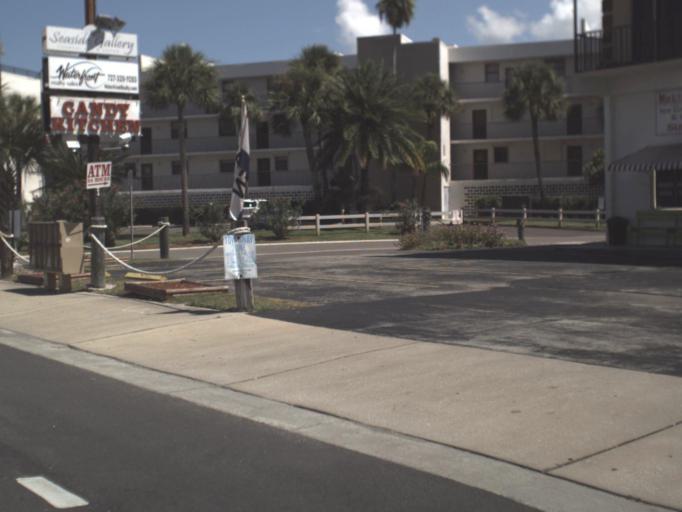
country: US
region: Florida
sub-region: Pinellas County
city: Redington Shores
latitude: 27.8333
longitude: -82.8335
